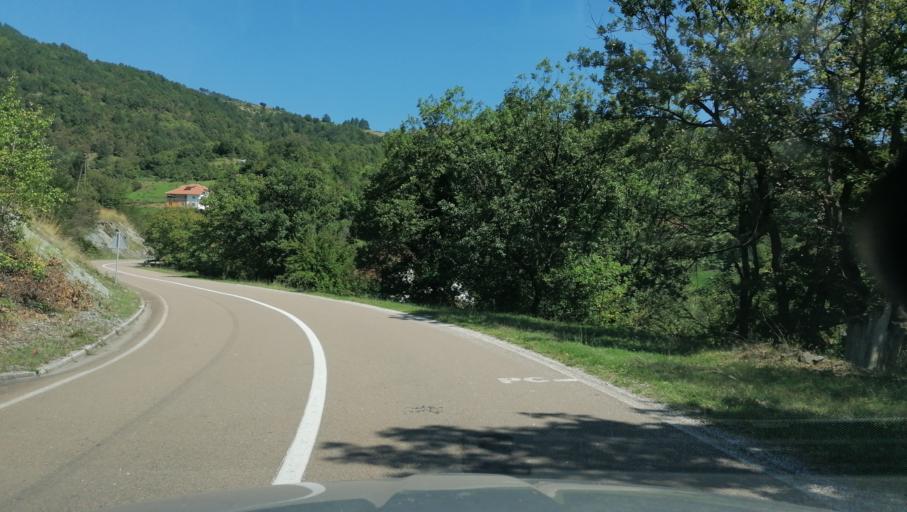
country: RS
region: Central Serbia
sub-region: Raski Okrug
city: Raska
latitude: 43.4687
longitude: 20.5535
